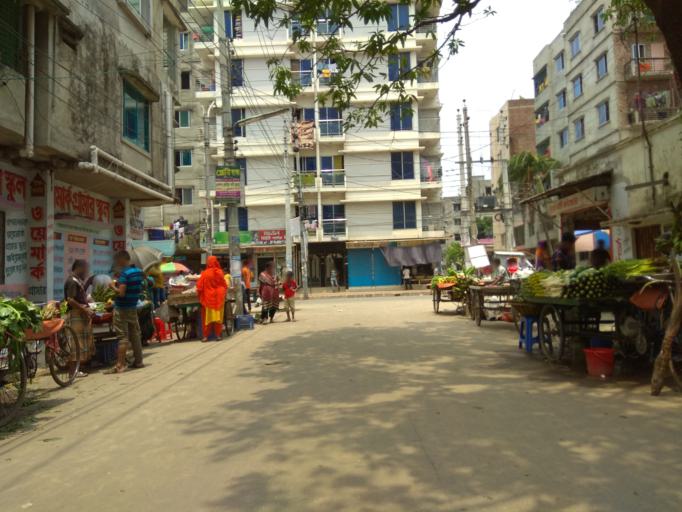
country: BD
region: Dhaka
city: Tungi
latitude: 23.8138
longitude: 90.3753
